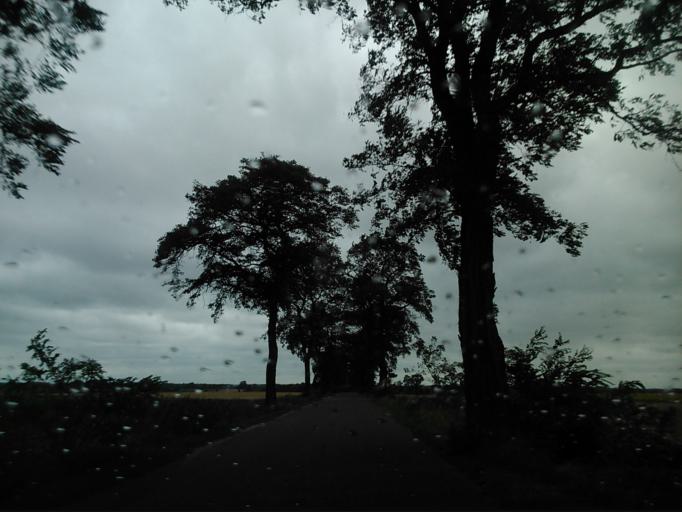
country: PL
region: Kujawsko-Pomorskie
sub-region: Powiat radziejowski
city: Piotrkow Kujawski
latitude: 52.5912
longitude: 18.4110
